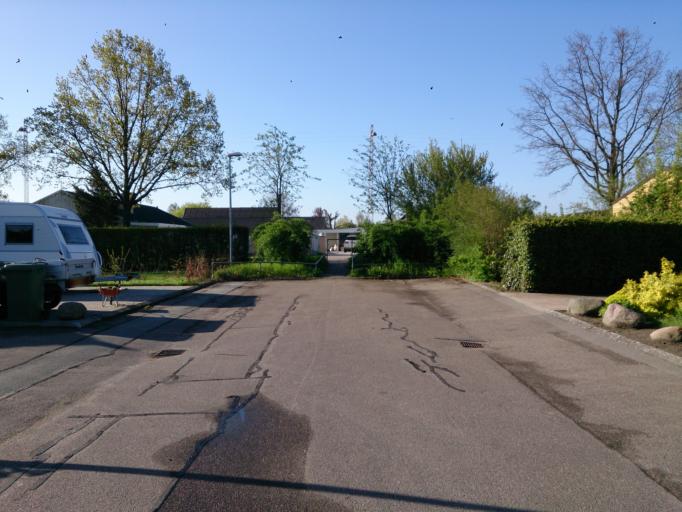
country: DK
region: Capital Region
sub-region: Tarnby Kommune
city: Tarnby
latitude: 55.6130
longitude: 12.5820
